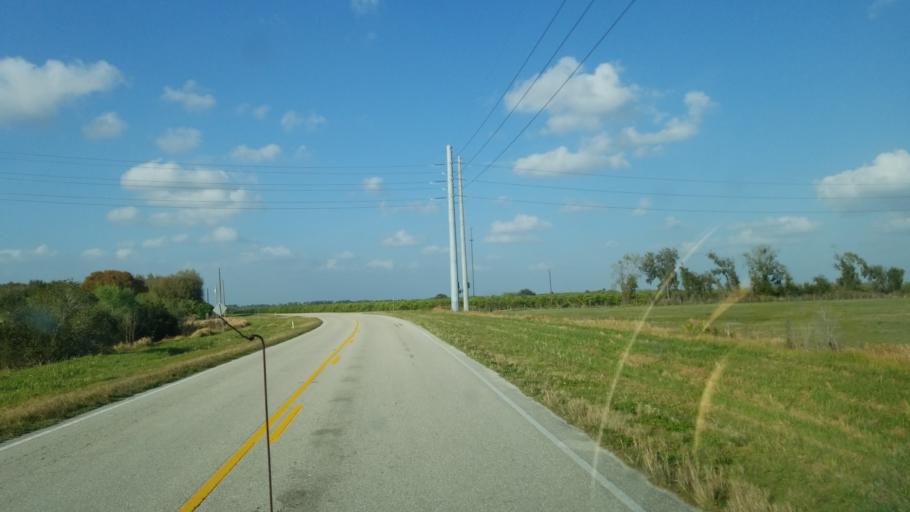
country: US
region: Florida
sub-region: Hardee County
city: Bowling Green
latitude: 27.5862
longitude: -81.9367
